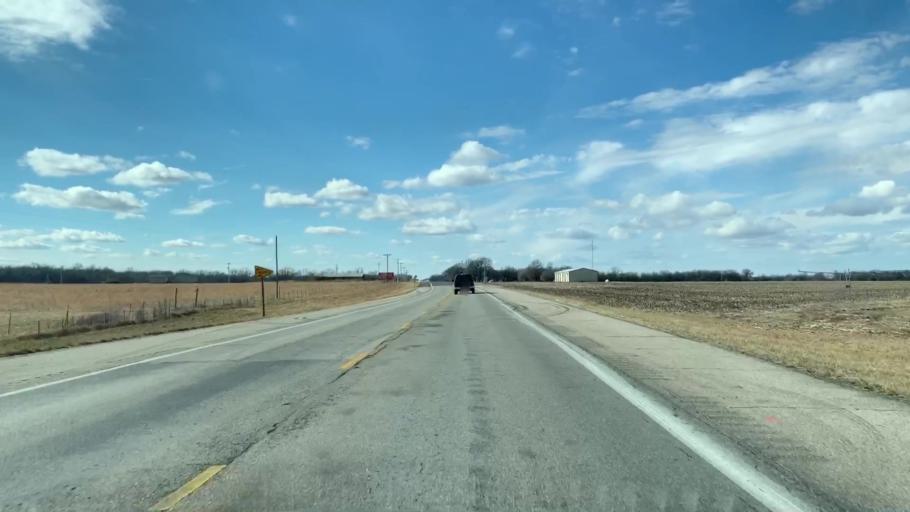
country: US
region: Kansas
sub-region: Labette County
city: Parsons
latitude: 37.3403
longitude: -95.1224
